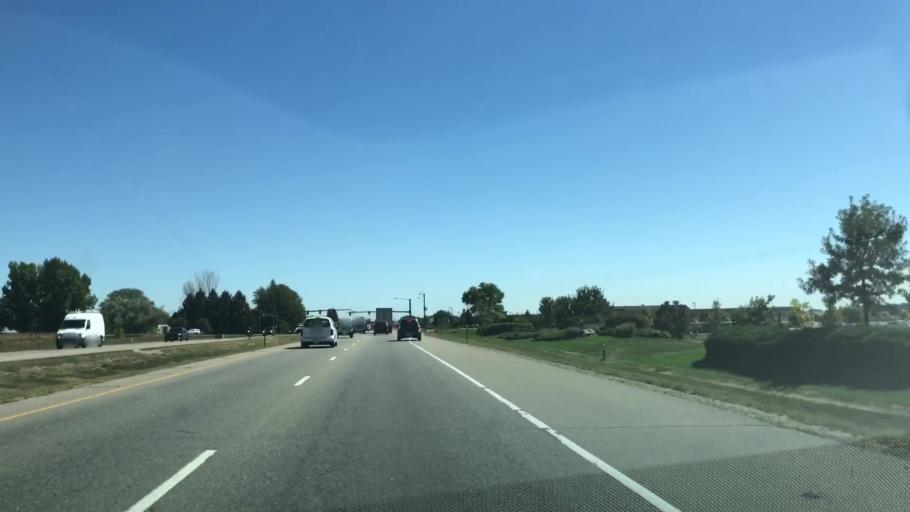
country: US
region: Colorado
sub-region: Weld County
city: Johnstown
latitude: 40.4072
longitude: -104.9770
